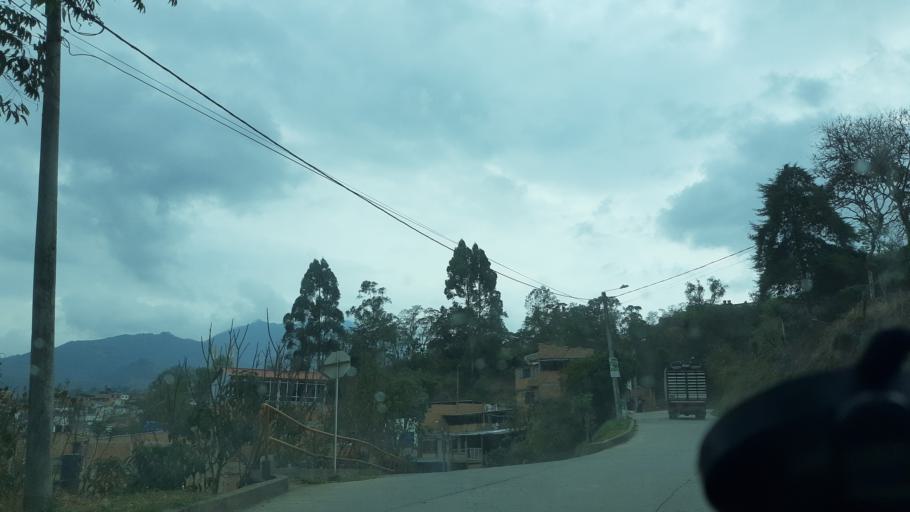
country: CO
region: Boyaca
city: Garagoa
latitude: 5.0786
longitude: -73.3680
